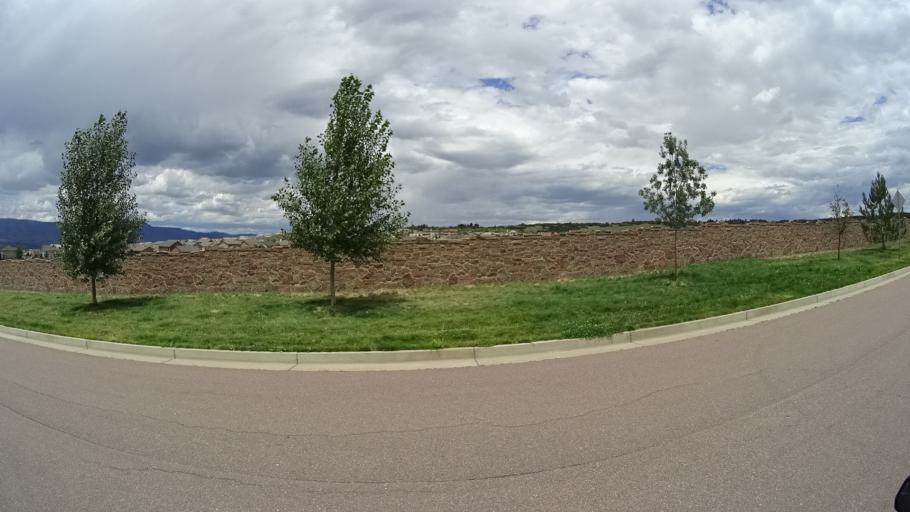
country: US
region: Colorado
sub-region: El Paso County
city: Gleneagle
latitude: 39.0219
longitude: -104.8058
